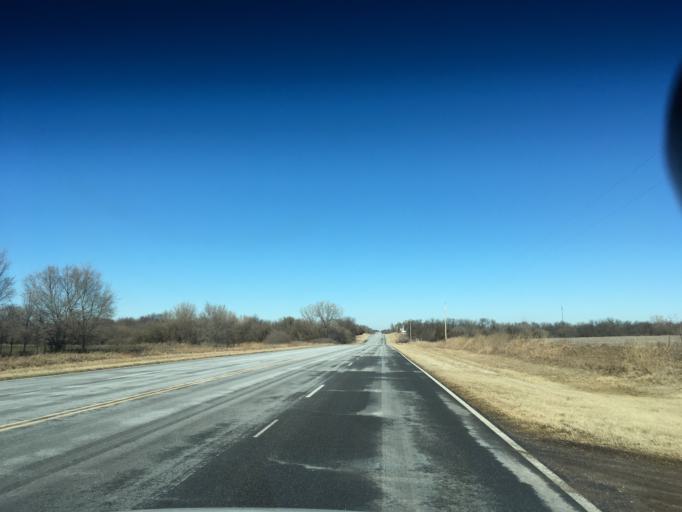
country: US
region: Kansas
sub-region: Harvey County
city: Sedgwick
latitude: 37.9301
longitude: -97.3363
